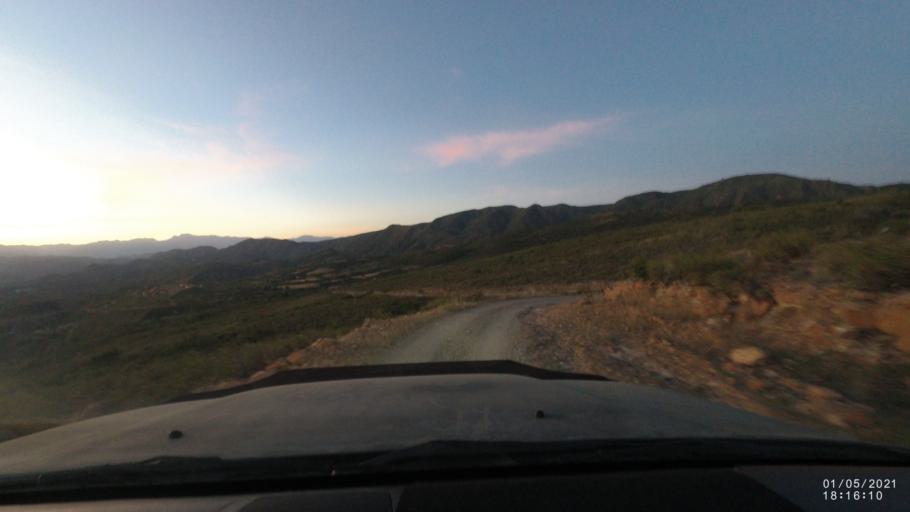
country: BO
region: Cochabamba
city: Capinota
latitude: -17.6727
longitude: -66.2178
